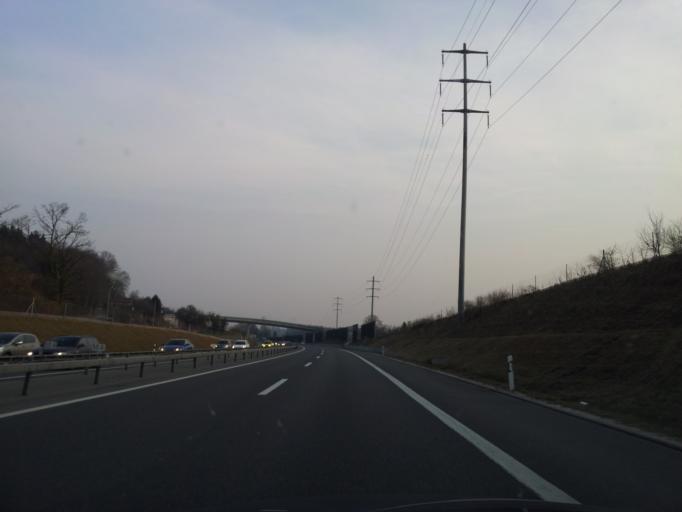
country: CH
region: Zurich
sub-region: Bezirk Affoltern
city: Obfelden / Toussen
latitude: 47.2615
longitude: 8.4414
